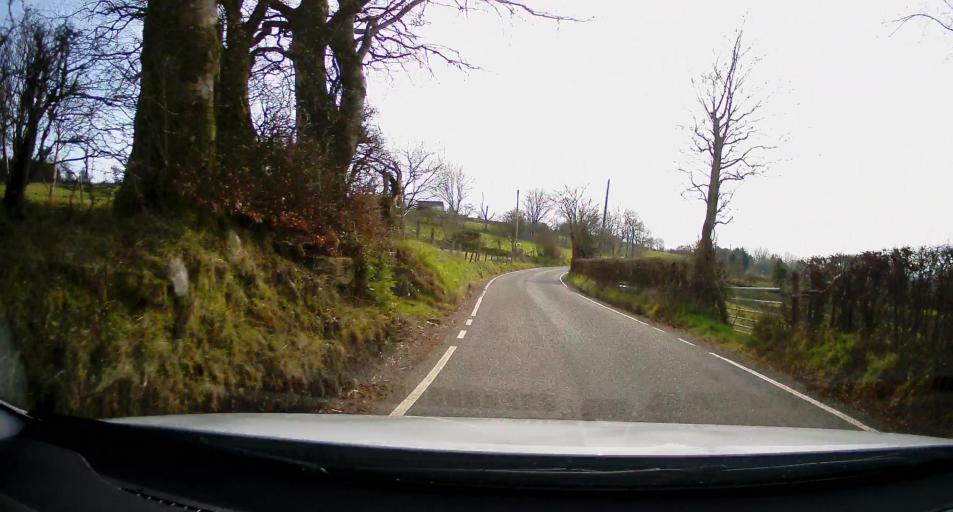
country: GB
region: Wales
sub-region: County of Ceredigion
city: Lledrod
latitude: 52.2580
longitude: -4.0780
